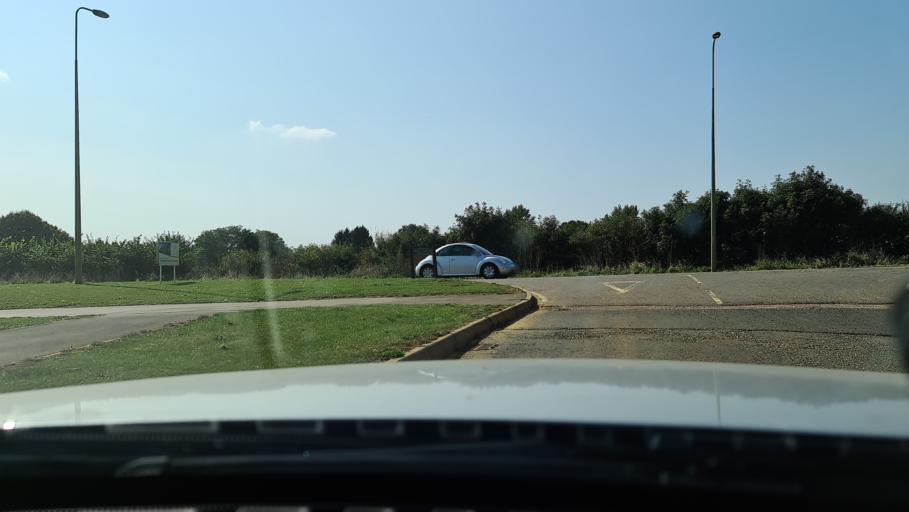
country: GB
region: England
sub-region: Oxfordshire
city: Hanwell
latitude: 52.0811
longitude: -1.3687
